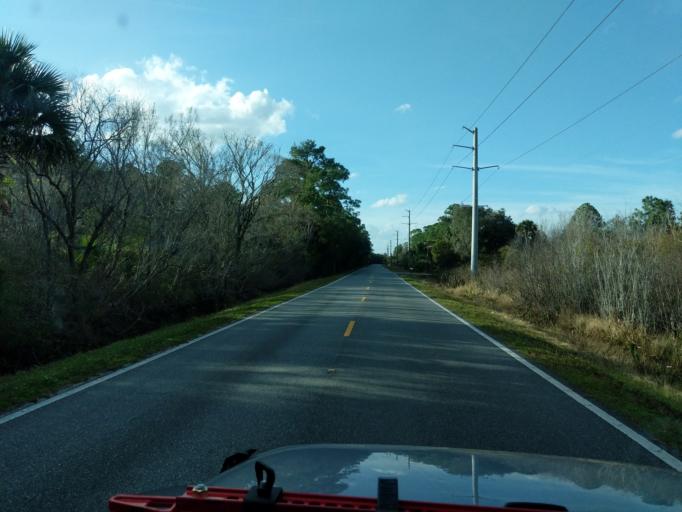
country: US
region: Florida
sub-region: Seminole County
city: Geneva
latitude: 28.7761
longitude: -81.1598
